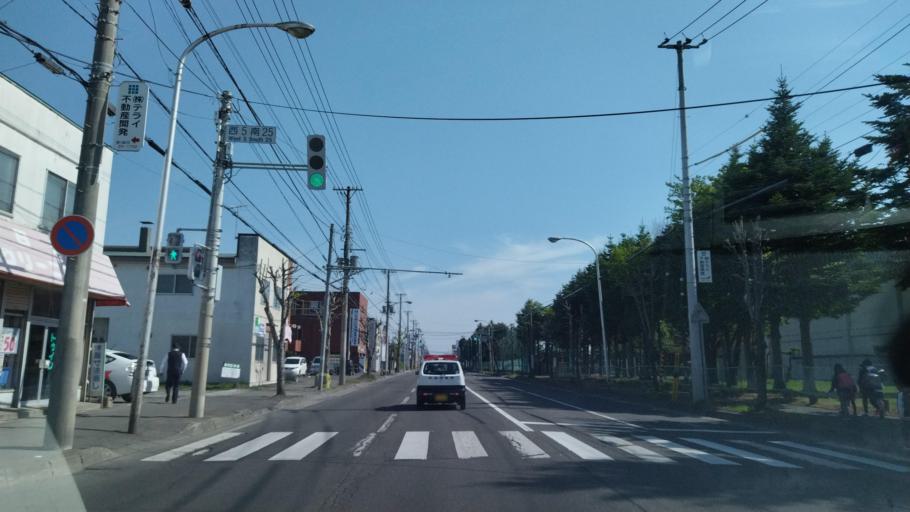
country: JP
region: Hokkaido
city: Obihiro
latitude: 42.9035
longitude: 143.1998
